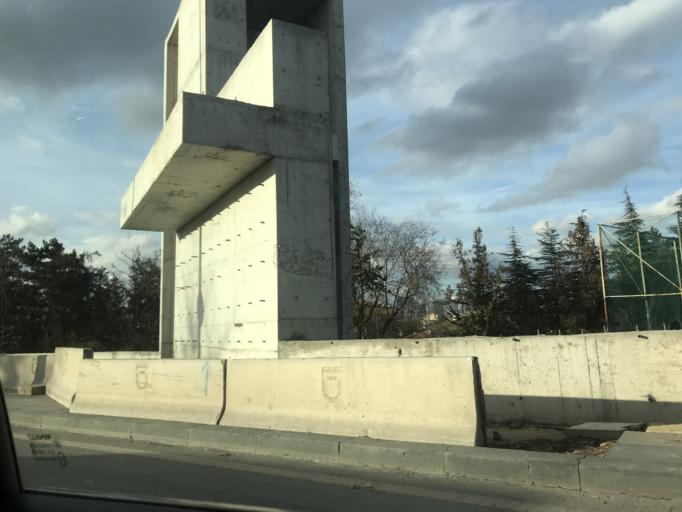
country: TR
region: Ankara
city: Ankara
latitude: 39.9594
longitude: 32.8641
